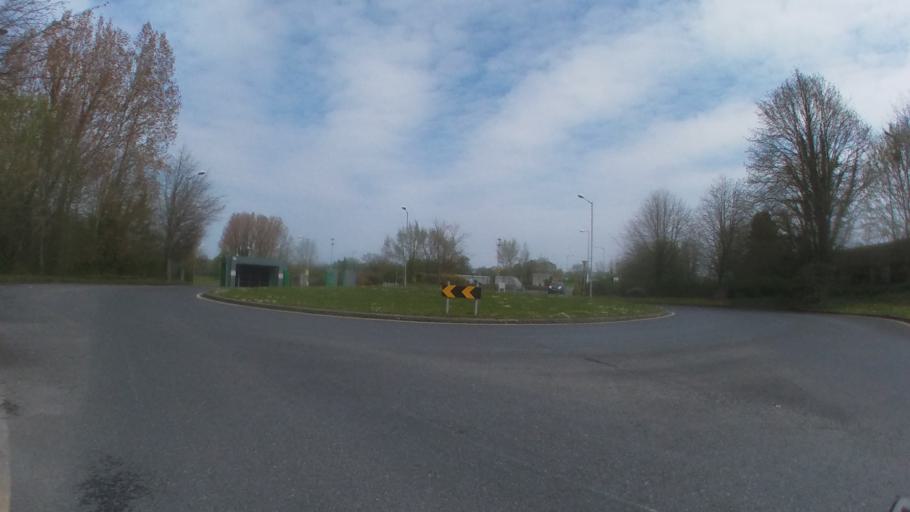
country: IE
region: Leinster
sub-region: Kilkenny
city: Kilkenny
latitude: 52.6458
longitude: -7.2160
